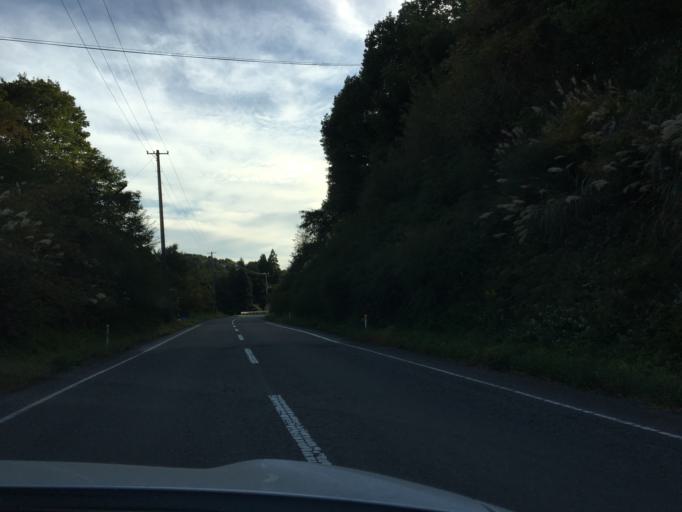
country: JP
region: Fukushima
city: Ishikawa
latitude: 37.2115
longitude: 140.5515
